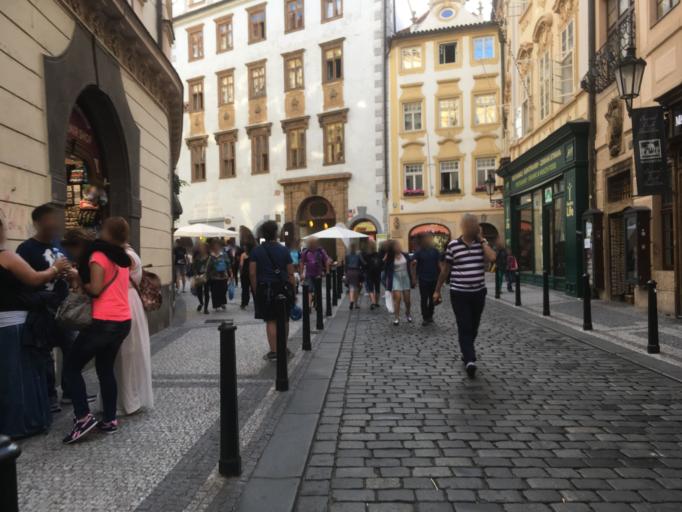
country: CZ
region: Praha
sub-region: Praha 1
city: Stare Mesto
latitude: 50.0860
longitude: 14.4207
